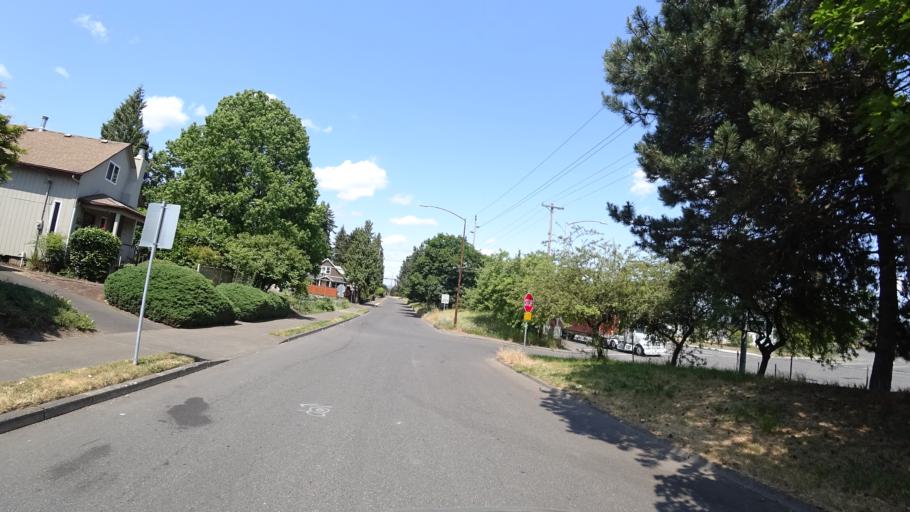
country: US
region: Oregon
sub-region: Washington County
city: West Haven
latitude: 45.6002
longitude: -122.7420
